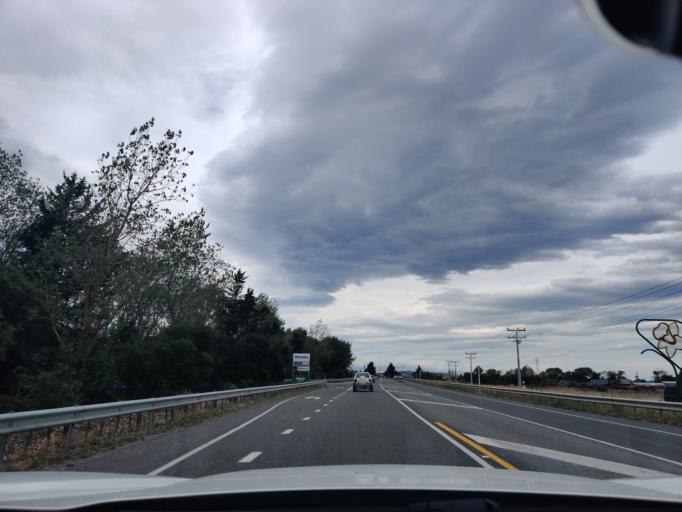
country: NZ
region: Wellington
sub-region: Masterton District
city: Masterton
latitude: -40.9673
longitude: 175.6056
